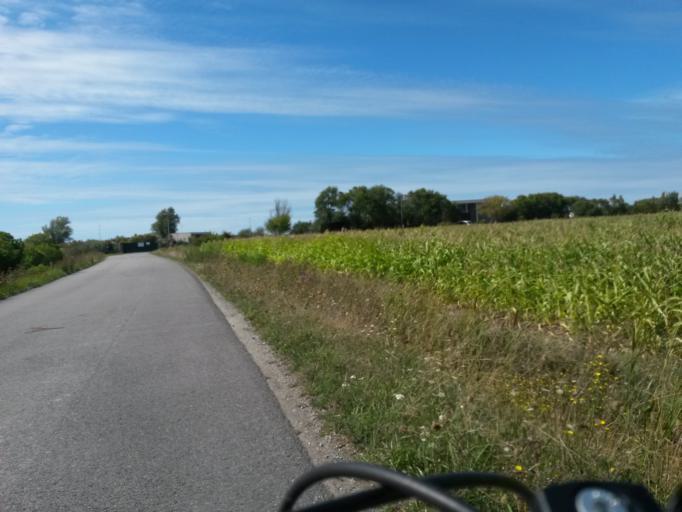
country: FR
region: Pays de la Loire
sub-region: Departement de la Loire-Atlantique
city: Guerande
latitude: 47.3041
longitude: -2.4329
